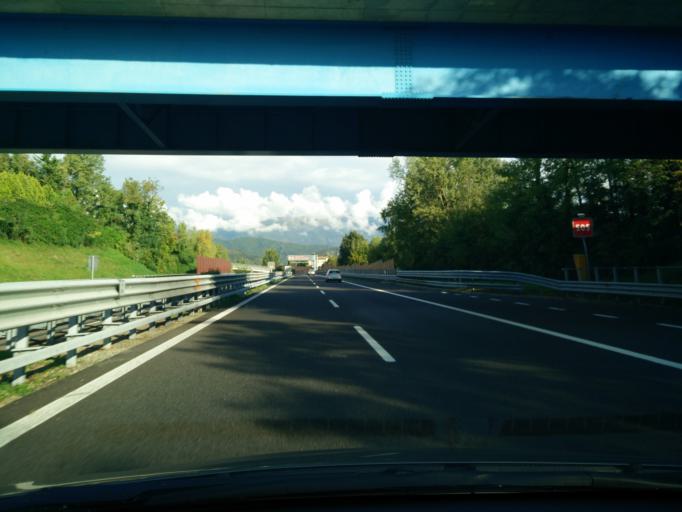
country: IT
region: Veneto
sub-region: Provincia di Treviso
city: Carpesica
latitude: 45.9551
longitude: 12.2925
